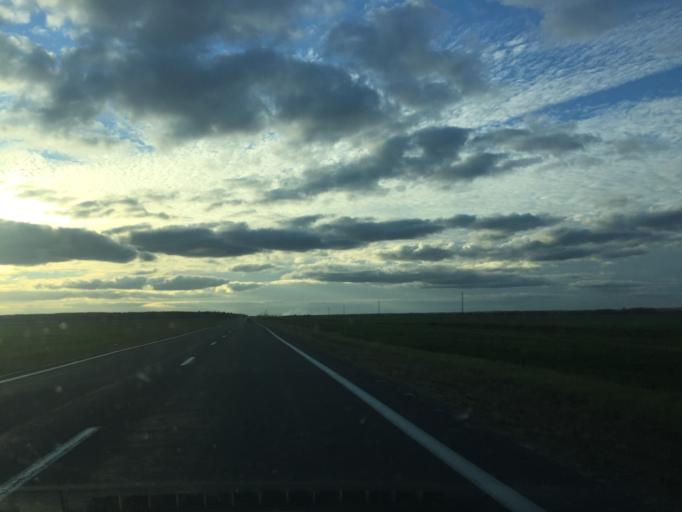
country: BY
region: Vitebsk
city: Vyerkhnyadzvinsk
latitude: 55.8250
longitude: 27.7859
